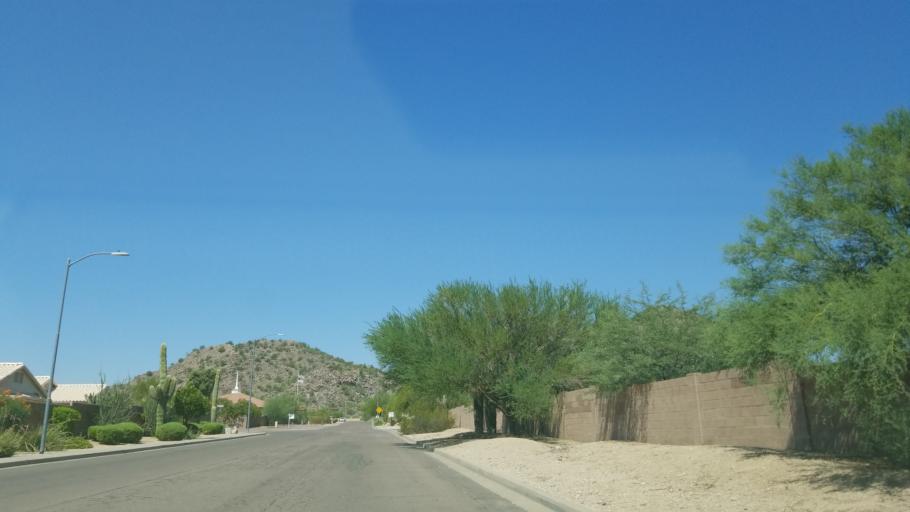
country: US
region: Arizona
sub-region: Maricopa County
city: Paradise Valley
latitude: 33.6770
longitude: -112.0357
